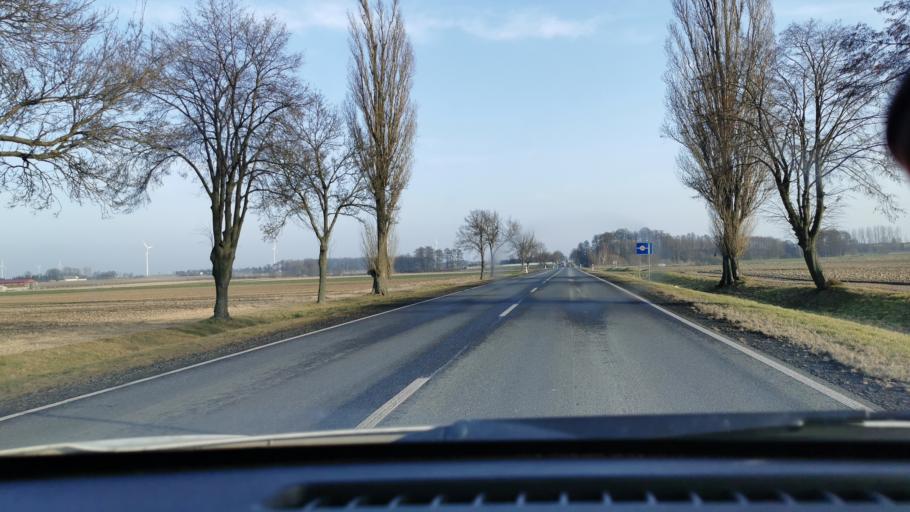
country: PL
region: Lodz Voivodeship
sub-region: Powiat sieradzki
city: Blaszki
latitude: 51.6425
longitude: 18.4901
